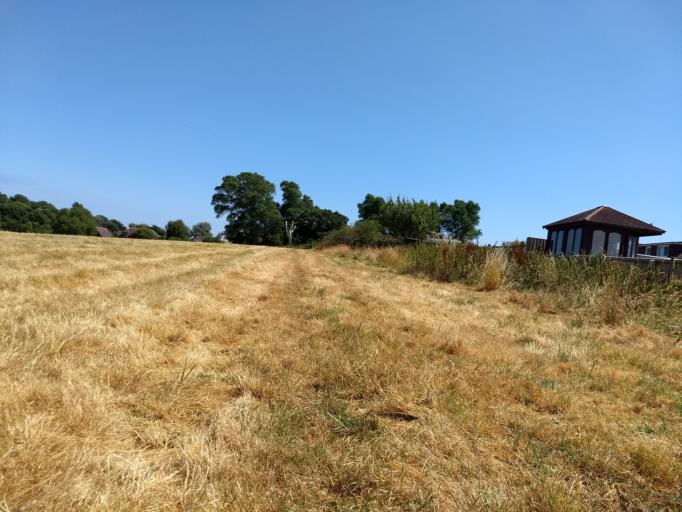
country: GB
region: England
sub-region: Isle of Wight
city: Brading
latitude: 50.6658
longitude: -1.1362
